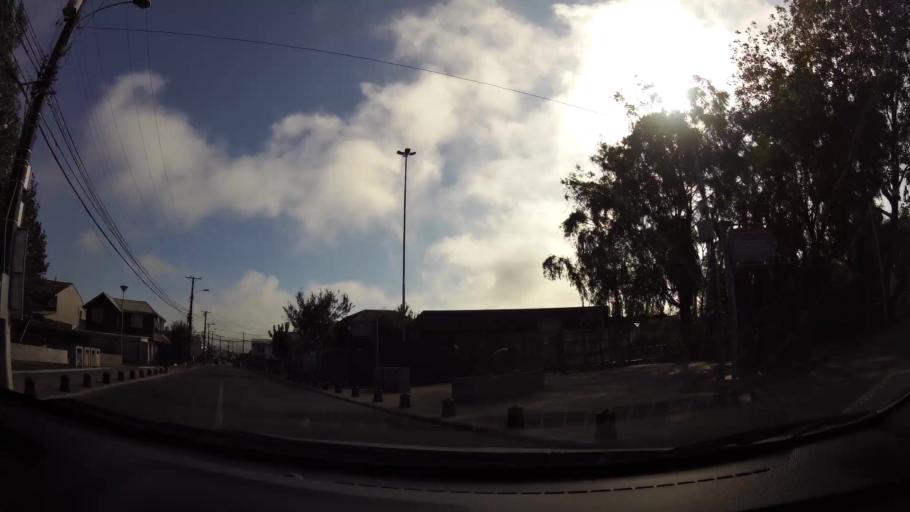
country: CL
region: Biobio
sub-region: Provincia de Concepcion
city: Concepcion
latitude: -36.7992
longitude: -73.0969
